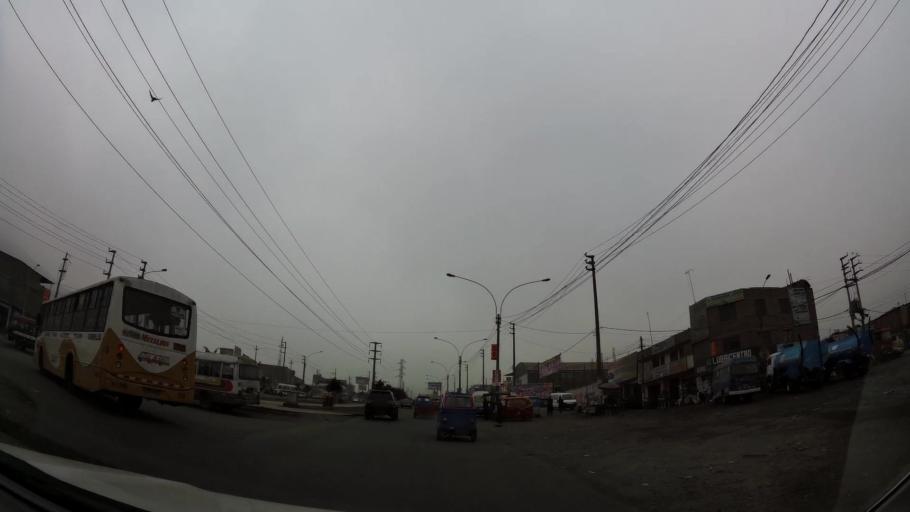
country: PE
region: Lima
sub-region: Lima
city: Urb. Santo Domingo
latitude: -11.9323
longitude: -76.9683
